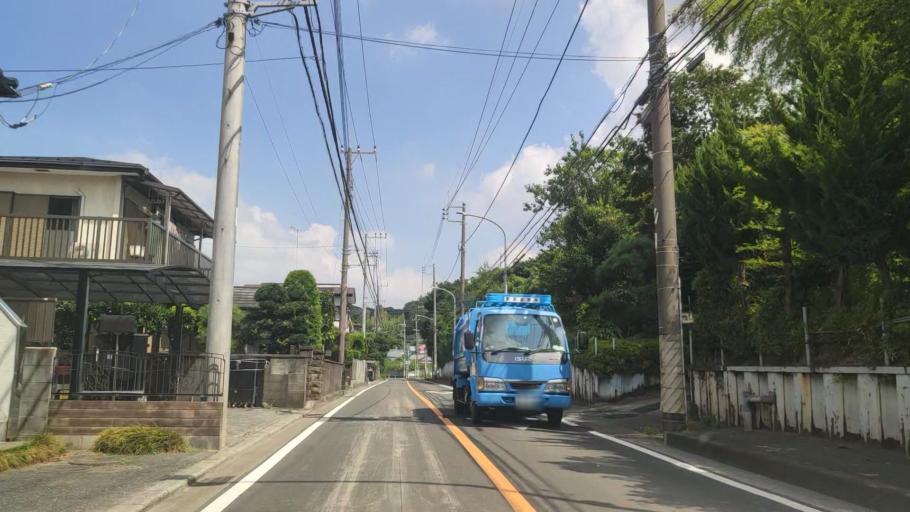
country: JP
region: Kanagawa
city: Minami-rinkan
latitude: 35.4414
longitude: 139.5074
